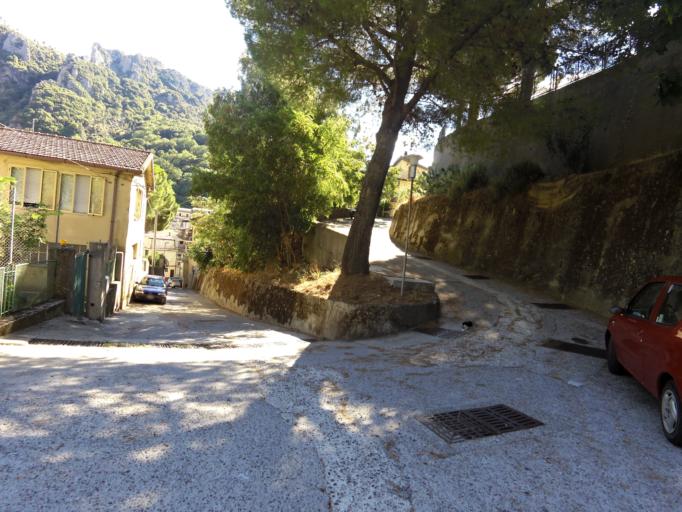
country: IT
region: Calabria
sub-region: Provincia di Reggio Calabria
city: Pazzano
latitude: 38.4778
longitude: 16.4527
